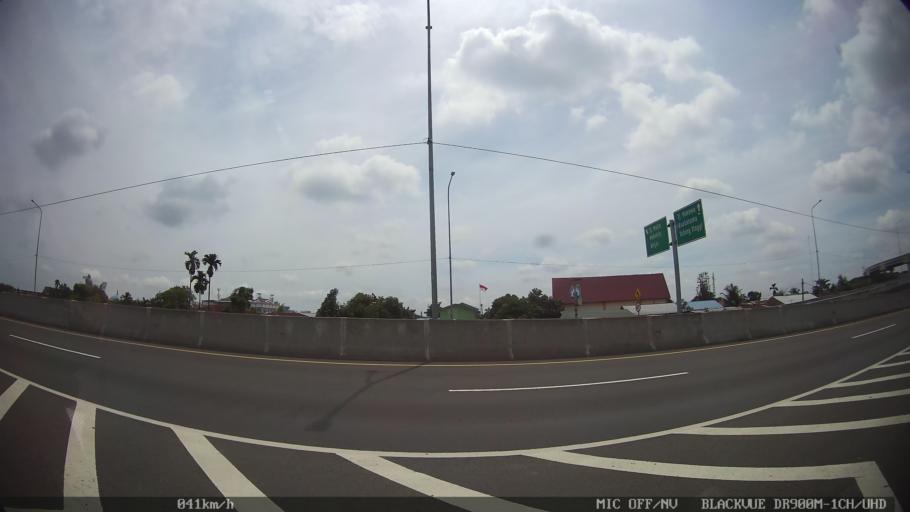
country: ID
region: North Sumatra
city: Medan
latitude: 3.6530
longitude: 98.6828
